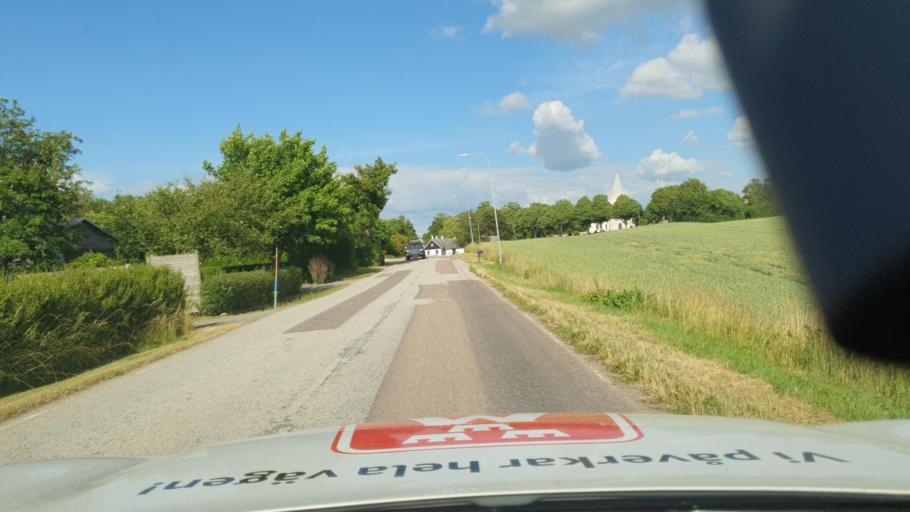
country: SE
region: Skane
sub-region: Skurups Kommun
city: Rydsgard
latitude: 55.4349
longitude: 13.6113
